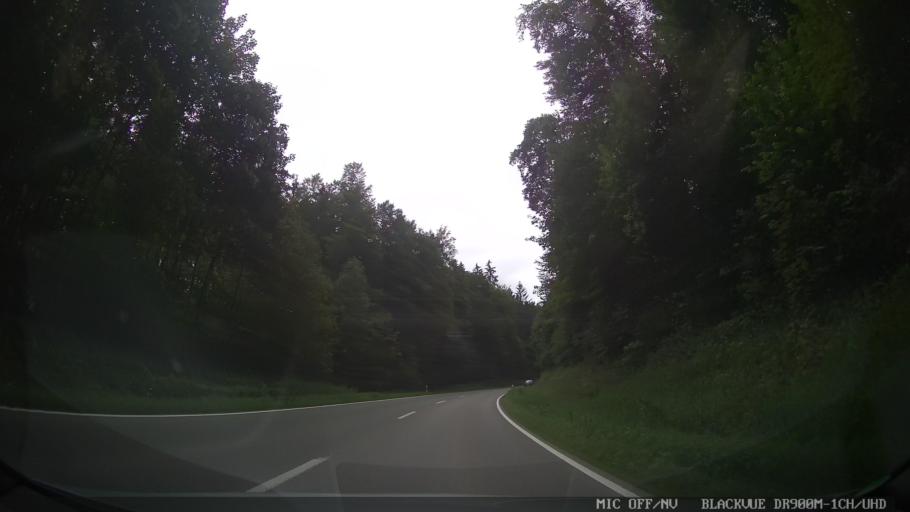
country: DE
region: Baden-Wuerttemberg
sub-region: Freiburg Region
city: Neuhausen ob Eck
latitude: 47.9862
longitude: 8.9298
